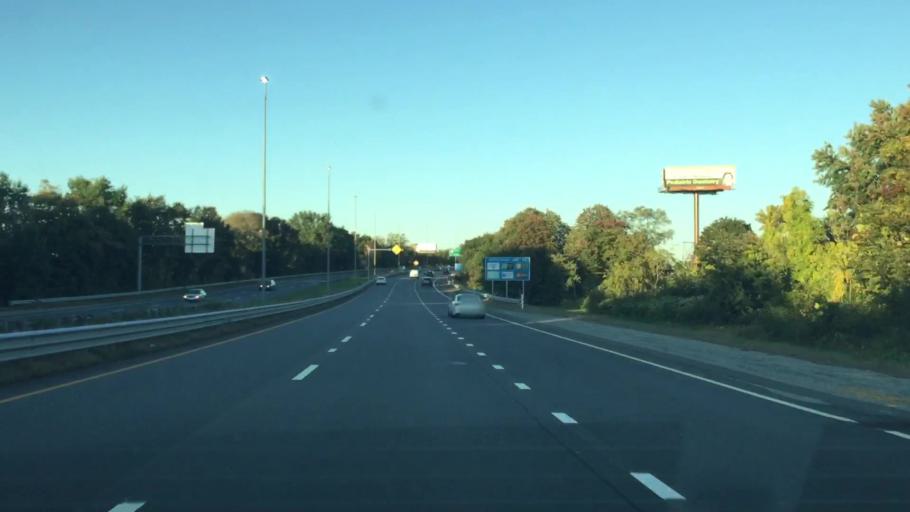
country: US
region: Massachusetts
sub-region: Middlesex County
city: Lowell
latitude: 42.6302
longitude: -71.3168
